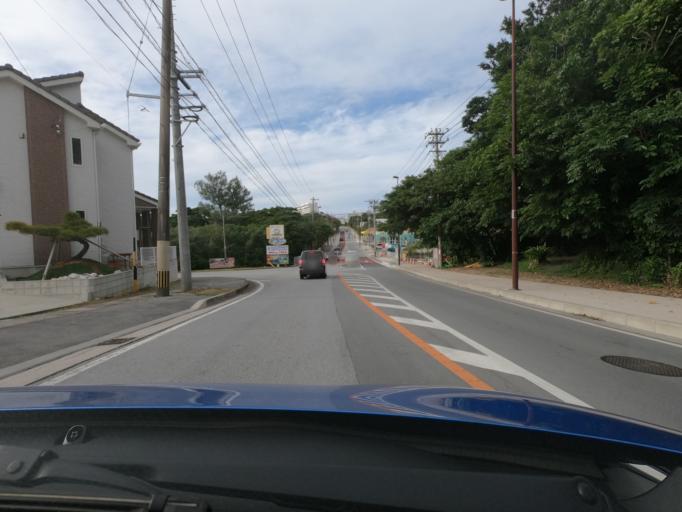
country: JP
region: Okinawa
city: Nago
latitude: 26.6781
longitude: 127.8886
